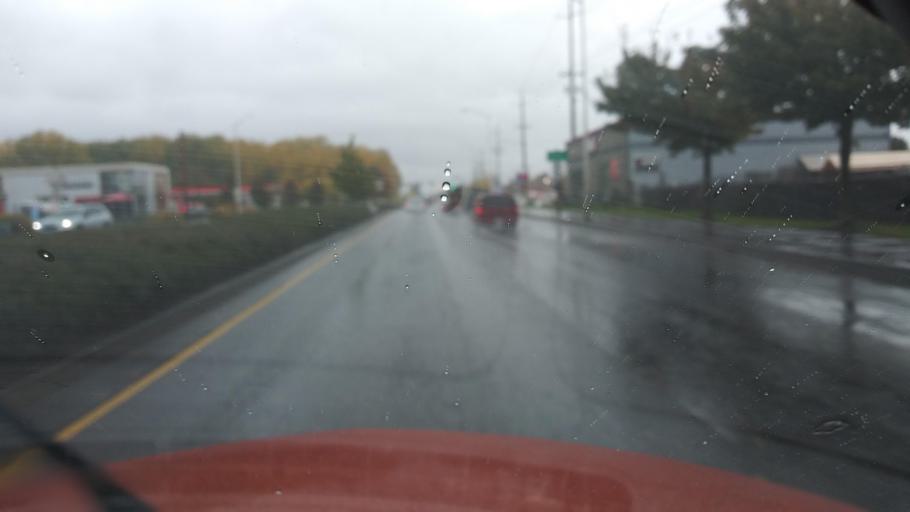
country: US
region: Oregon
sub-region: Washington County
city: Cornelius
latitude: 45.5202
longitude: -123.0468
